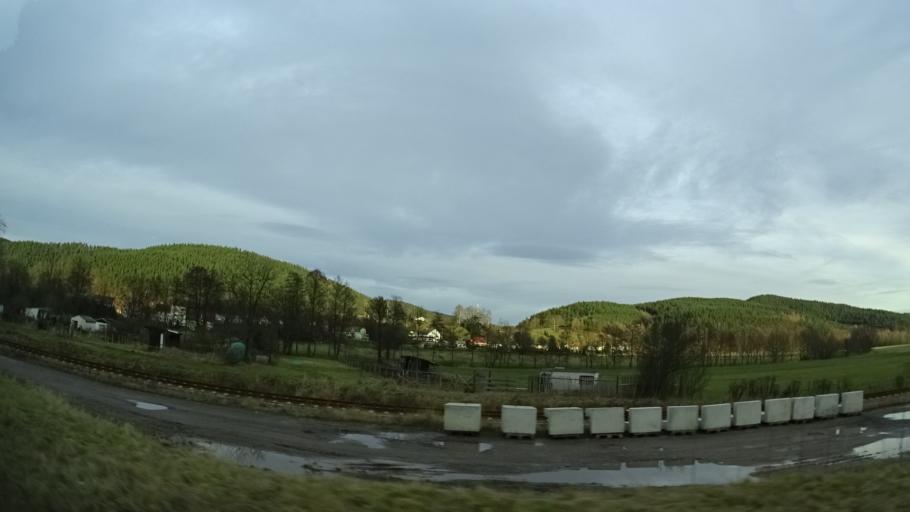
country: DE
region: Thuringia
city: Langenorla
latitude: 50.7295
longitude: 11.5934
